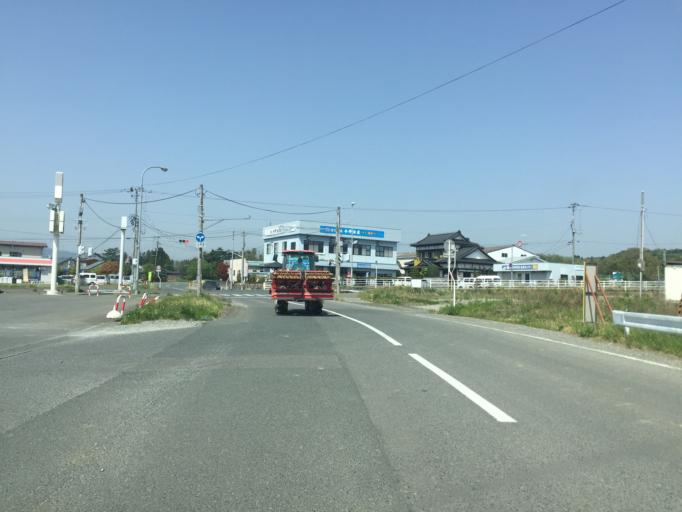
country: JP
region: Miyagi
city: Marumori
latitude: 37.7703
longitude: 140.9444
